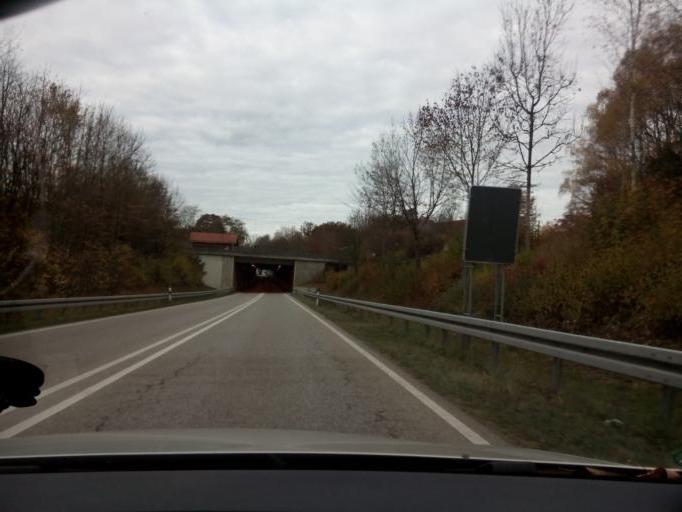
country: DE
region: Bavaria
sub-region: Upper Bavaria
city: Oberhaching
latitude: 48.0355
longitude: 11.5778
